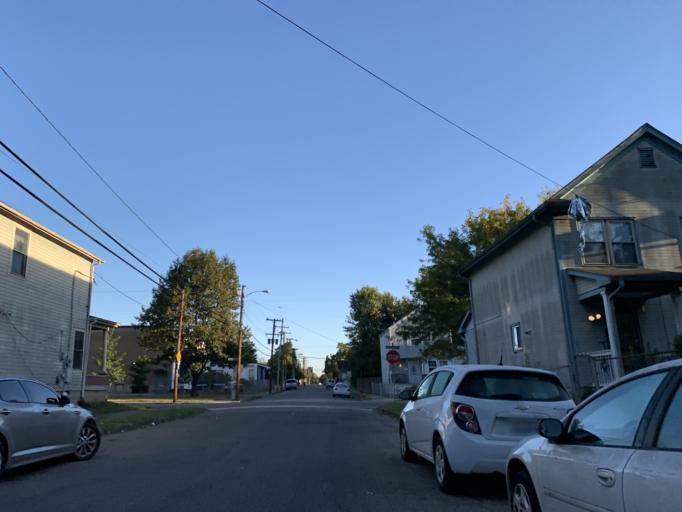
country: US
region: Kentucky
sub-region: Jefferson County
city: Louisville
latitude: 38.2382
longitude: -85.7807
